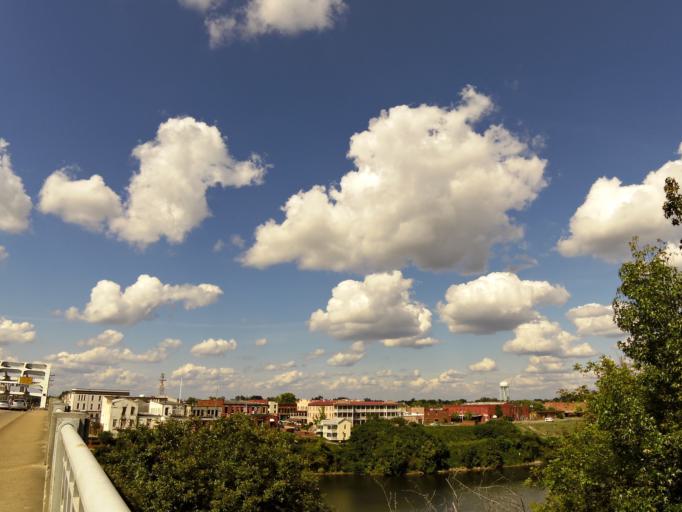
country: US
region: Alabama
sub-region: Dallas County
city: Selma
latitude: 32.4045
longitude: -87.0179
